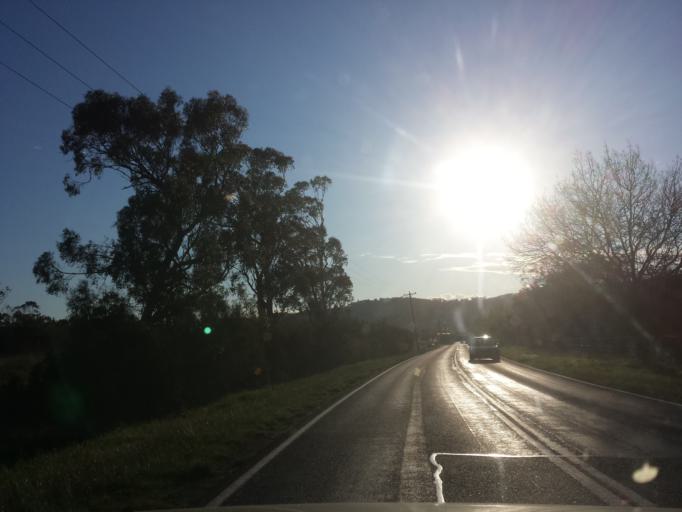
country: AU
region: Victoria
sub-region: Yarra Ranges
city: Yarra Glen
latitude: -37.6597
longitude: 145.3863
